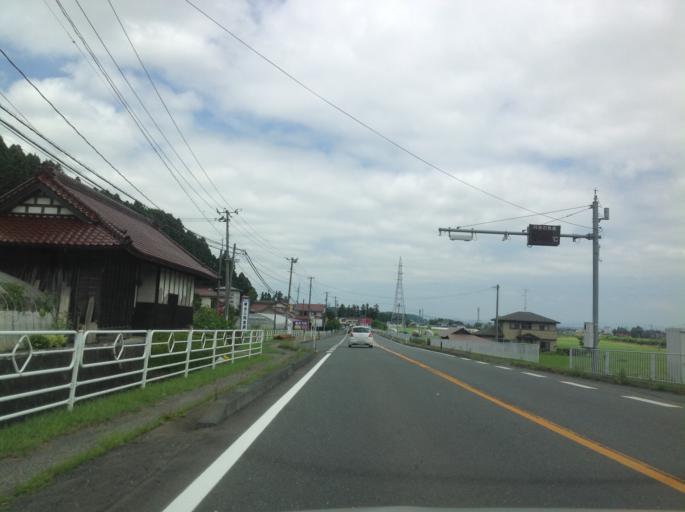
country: JP
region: Iwate
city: Mizusawa
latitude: 39.0849
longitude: 141.1364
